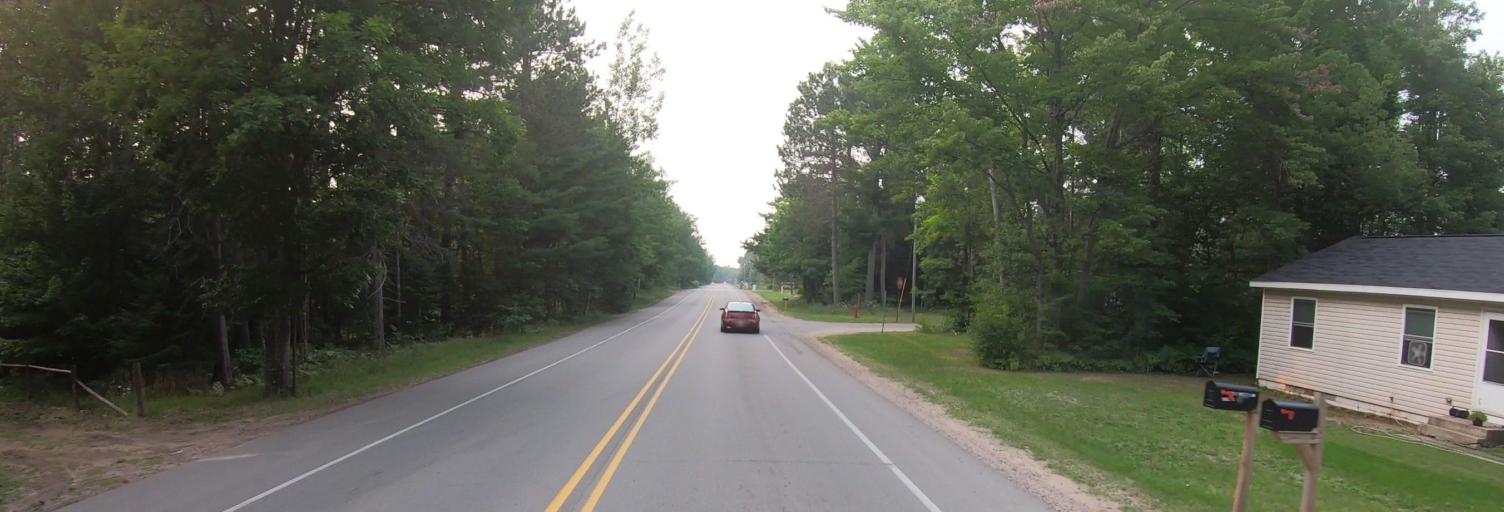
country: US
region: Michigan
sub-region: Chippewa County
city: Sault Ste. Marie
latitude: 46.4579
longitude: -84.6147
